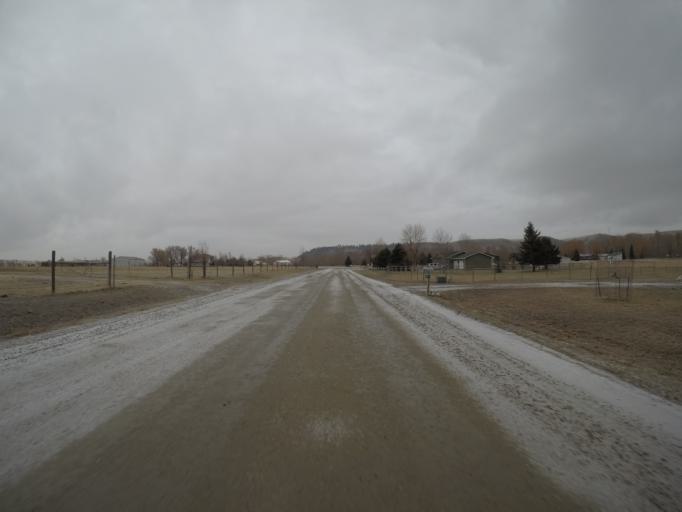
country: US
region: Montana
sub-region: Stillwater County
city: Absarokee
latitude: 45.5296
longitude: -109.4488
